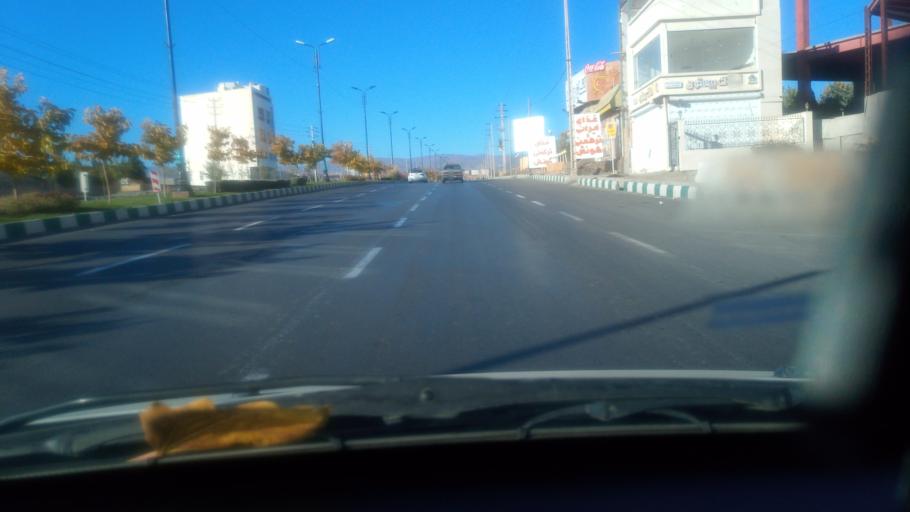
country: IR
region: Razavi Khorasan
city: Torqabeh
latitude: 36.3190
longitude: 59.3917
